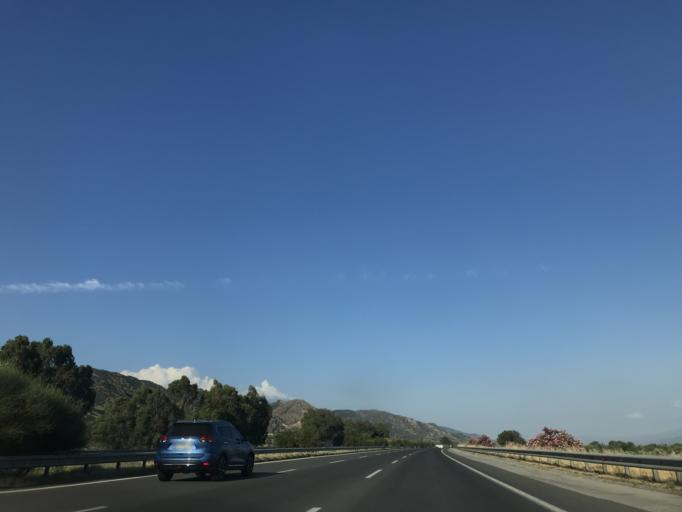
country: TR
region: Aydin
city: Incirliova
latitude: 37.8762
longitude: 27.6861
